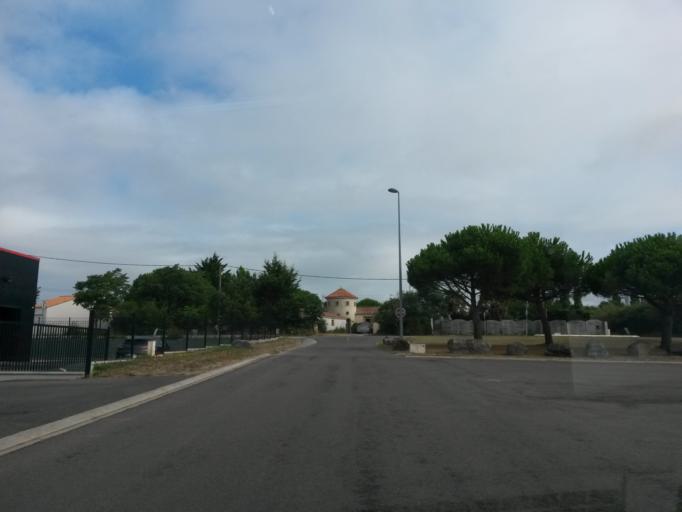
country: FR
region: Pays de la Loire
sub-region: Departement de la Vendee
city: Olonne-sur-Mer
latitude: 46.5226
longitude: -1.7845
